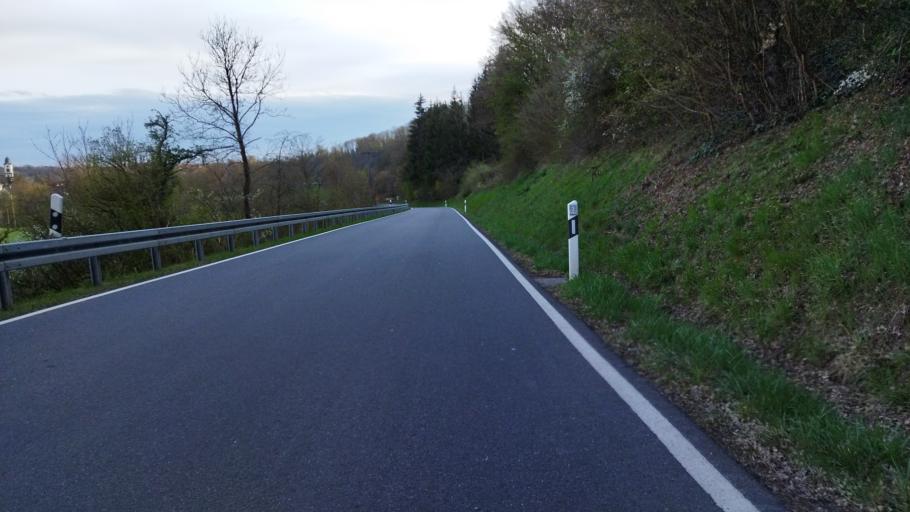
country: DE
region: Baden-Wuerttemberg
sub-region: Regierungsbezirk Stuttgart
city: Oedheim
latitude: 49.2748
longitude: 9.2225
